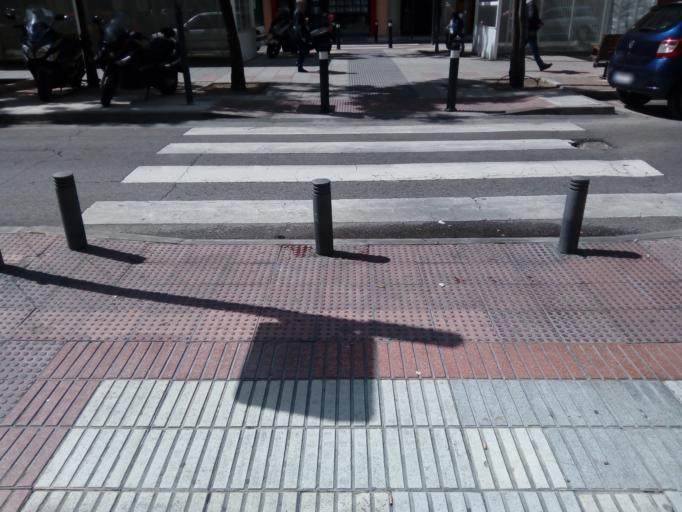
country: ES
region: Madrid
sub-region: Provincia de Madrid
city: Retiro
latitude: 40.4183
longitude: -3.6754
